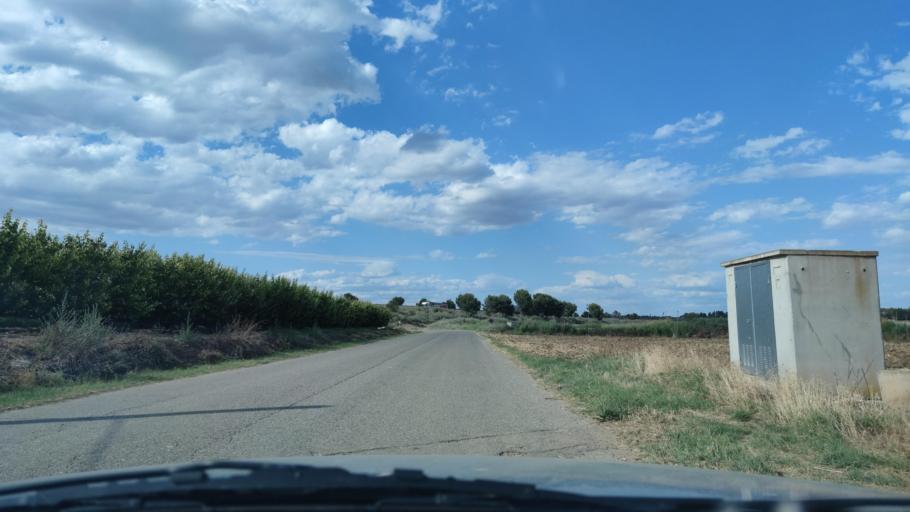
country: ES
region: Catalonia
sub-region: Provincia de Lleida
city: Alcarras
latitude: 41.6009
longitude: 0.5287
